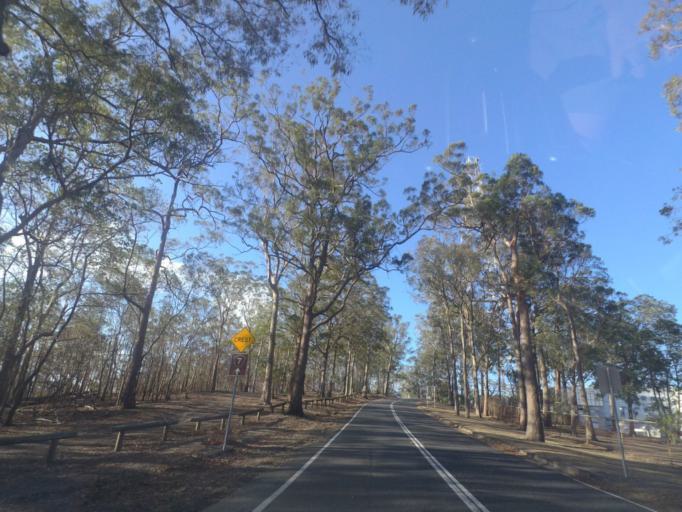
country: AU
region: Queensland
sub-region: Brisbane
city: Kenmore Hills
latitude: -27.4676
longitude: 152.9430
